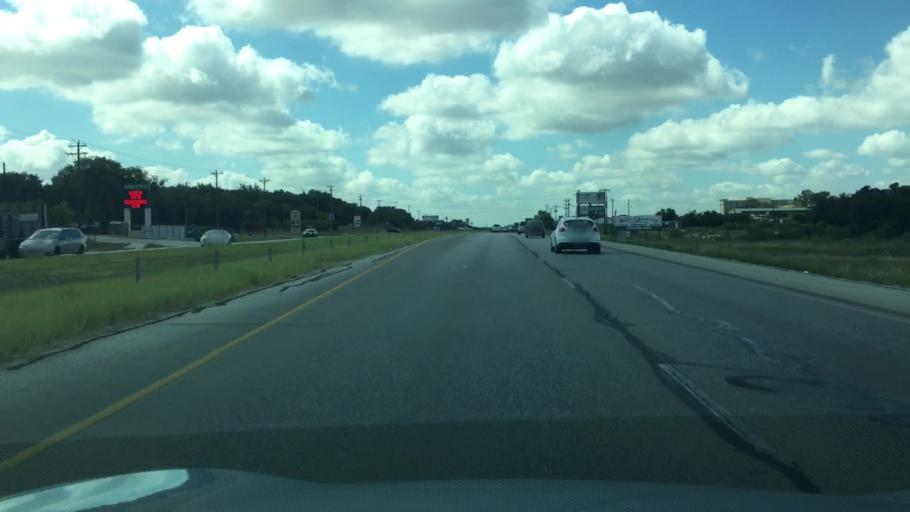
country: US
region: Texas
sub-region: Comal County
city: Bulverde
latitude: 29.8134
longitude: -98.4186
